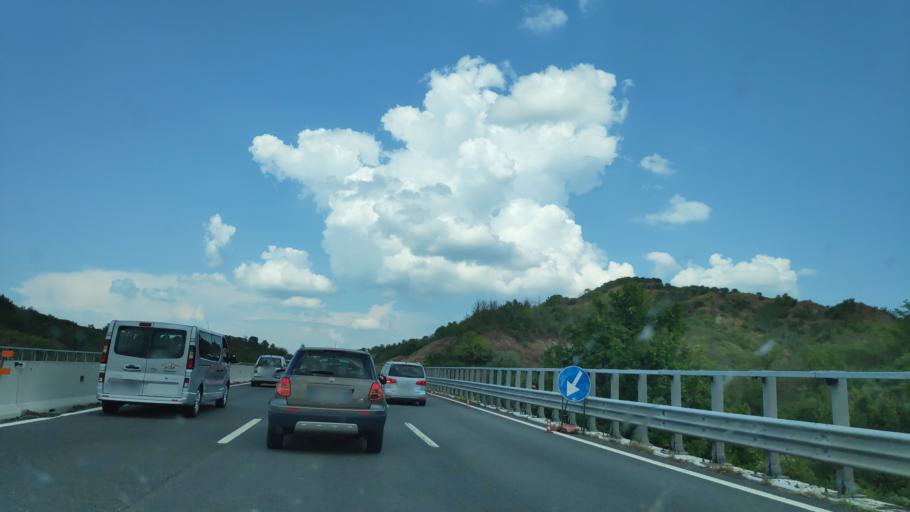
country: IT
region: Umbria
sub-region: Provincia di Terni
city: Ficulle
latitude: 42.8311
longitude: 12.0428
